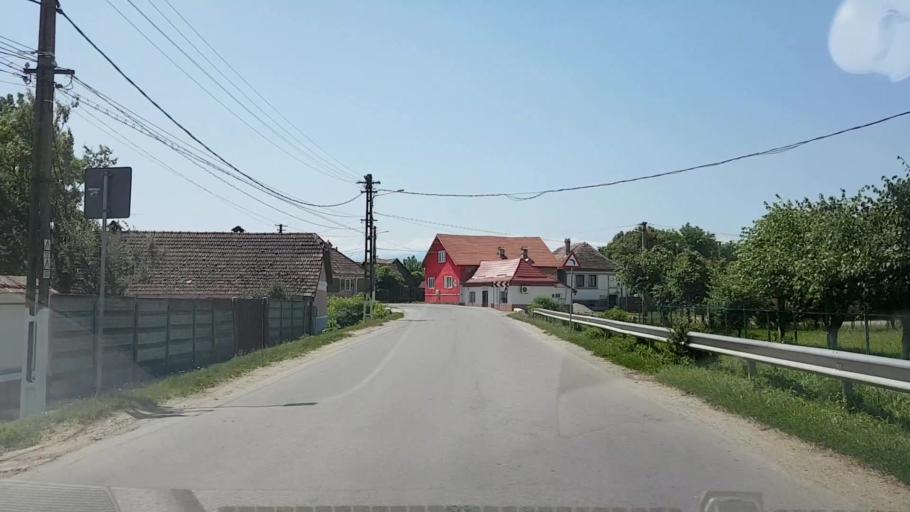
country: RO
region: Brasov
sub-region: Comuna Cincu
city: Cincu
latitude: 45.9135
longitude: 24.8075
